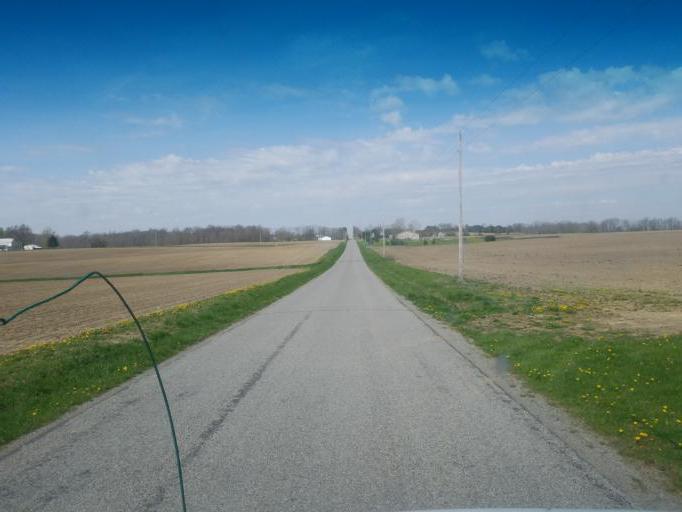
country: US
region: Ohio
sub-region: Logan County
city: Northwood
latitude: 40.4978
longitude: -83.6630
